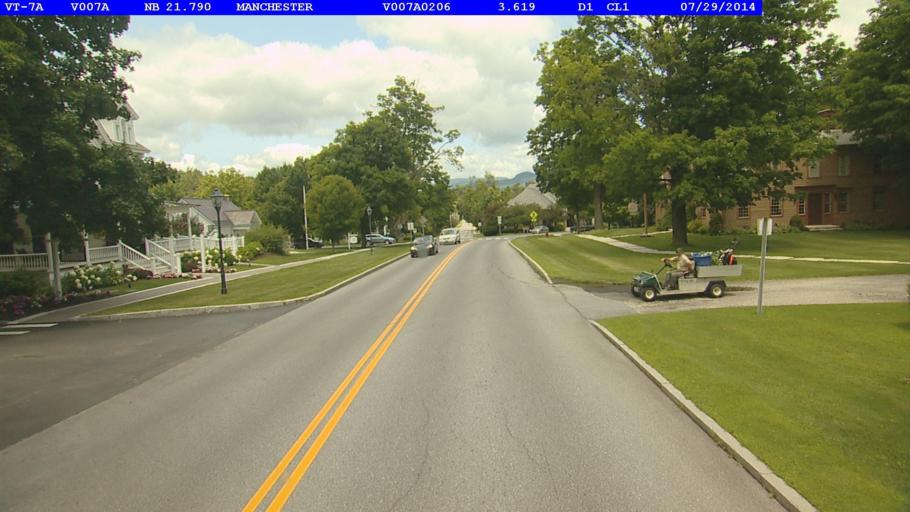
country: US
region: Vermont
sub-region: Bennington County
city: Manchester Center
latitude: 43.1628
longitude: -73.0721
